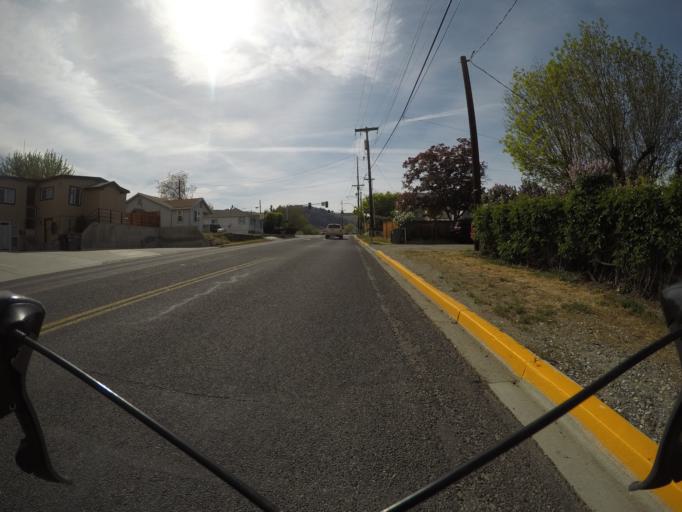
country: US
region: Washington
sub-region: Douglas County
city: East Wenatchee
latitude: 47.4045
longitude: -120.3021
